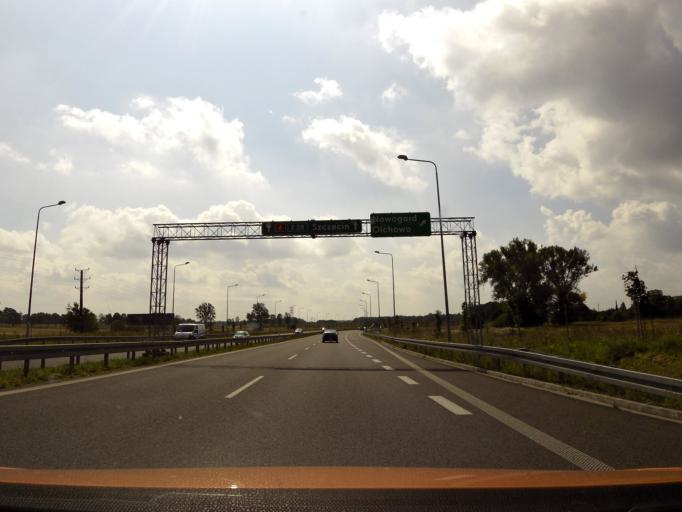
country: PL
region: West Pomeranian Voivodeship
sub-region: Powiat goleniowski
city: Nowogard
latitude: 53.6603
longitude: 15.0772
